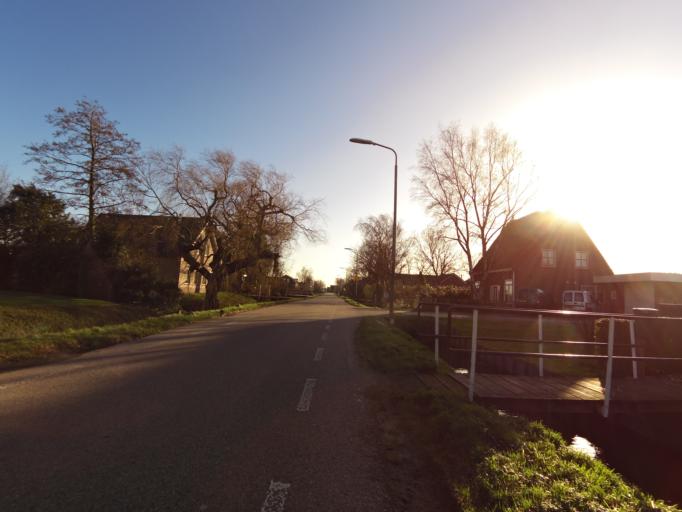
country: NL
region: South Holland
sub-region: Gemeente Pijnacker-Nootdorp
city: Pijnacker
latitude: 52.0109
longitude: 4.4252
